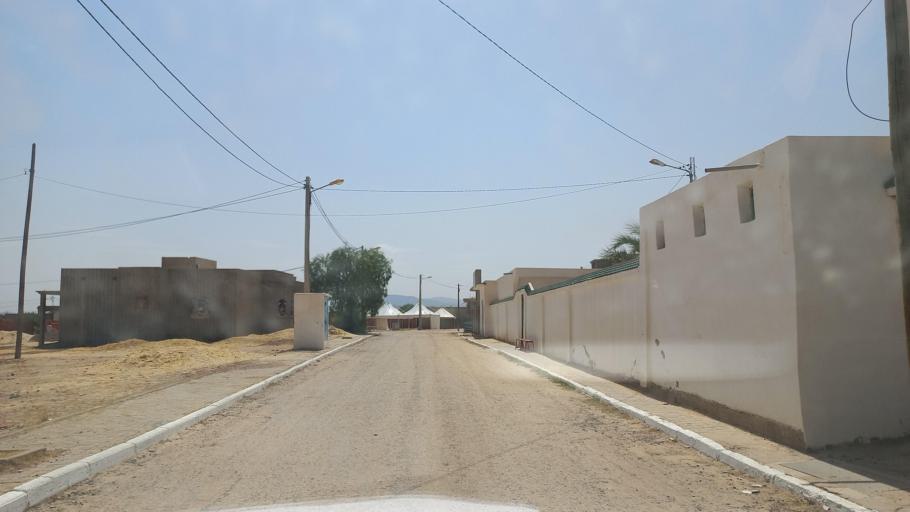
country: TN
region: Al Qasrayn
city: Kasserine
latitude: 35.2519
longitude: 9.0256
